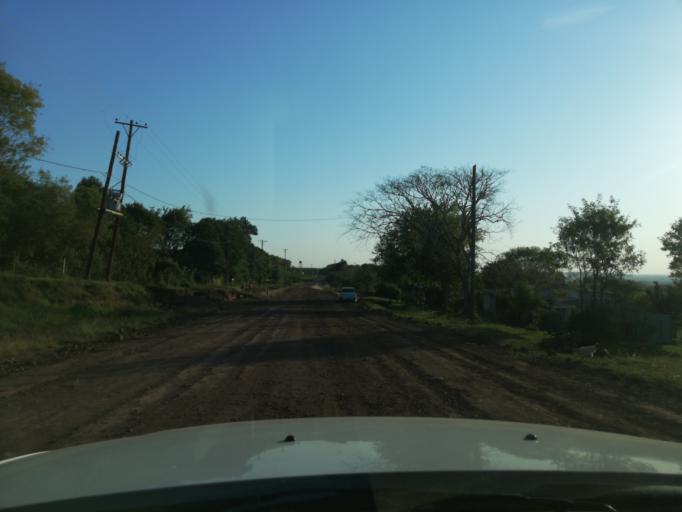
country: AR
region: Misiones
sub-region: Departamento de Apostoles
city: San Jose
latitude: -27.6310
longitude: -55.7272
